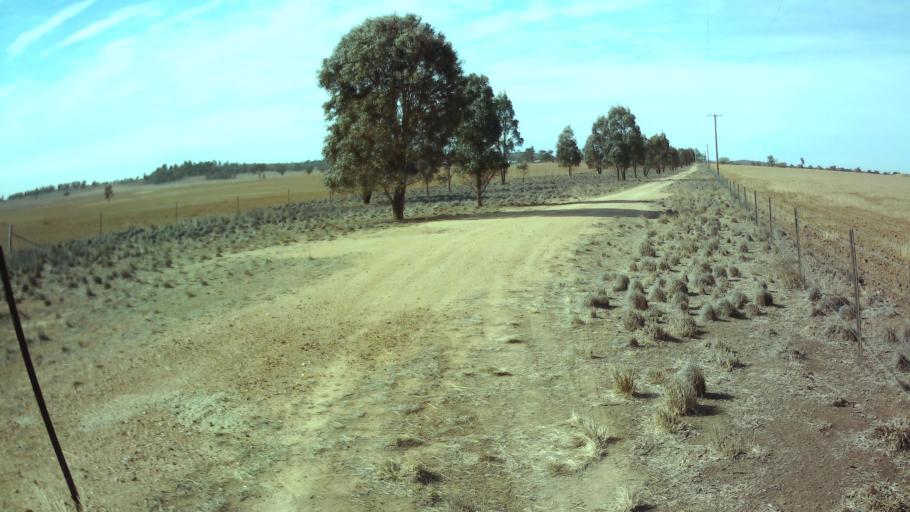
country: AU
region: New South Wales
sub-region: Weddin
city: Grenfell
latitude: -33.7340
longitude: 148.0085
